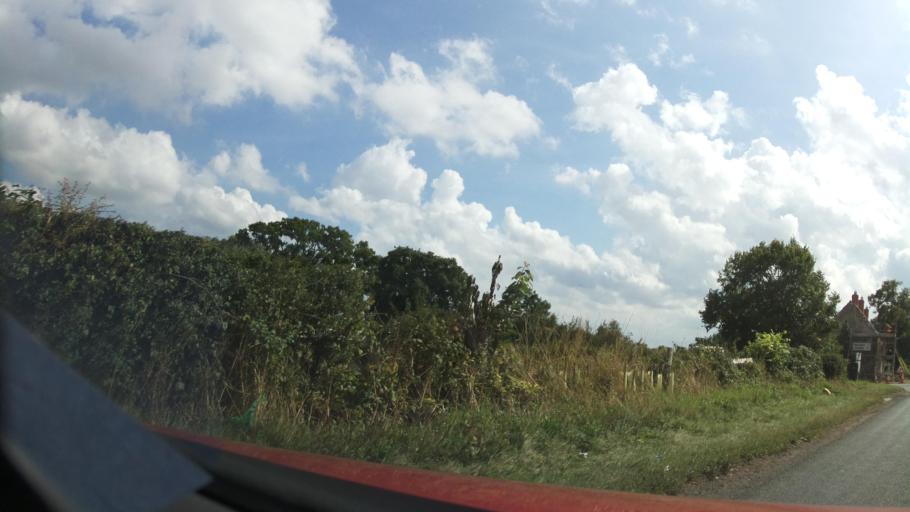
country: GB
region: England
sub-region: Darlington
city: High Coniscliffe
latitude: 54.5185
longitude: -1.6717
